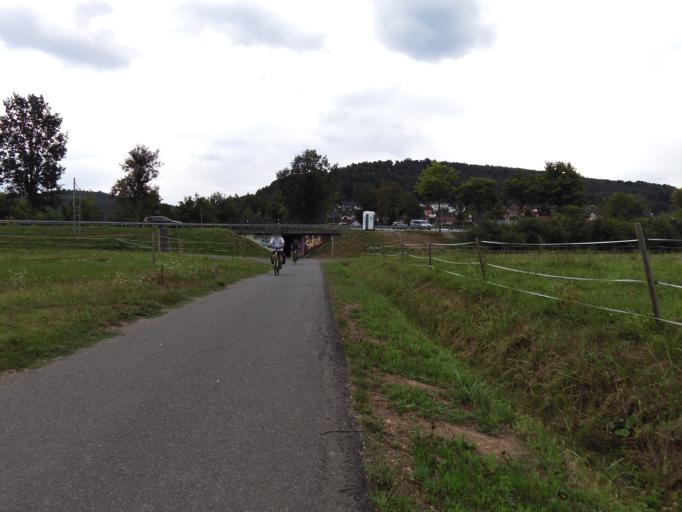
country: DE
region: Hesse
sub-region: Regierungsbezirk Darmstadt
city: Lutzelbach
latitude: 49.8159
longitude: 9.0442
